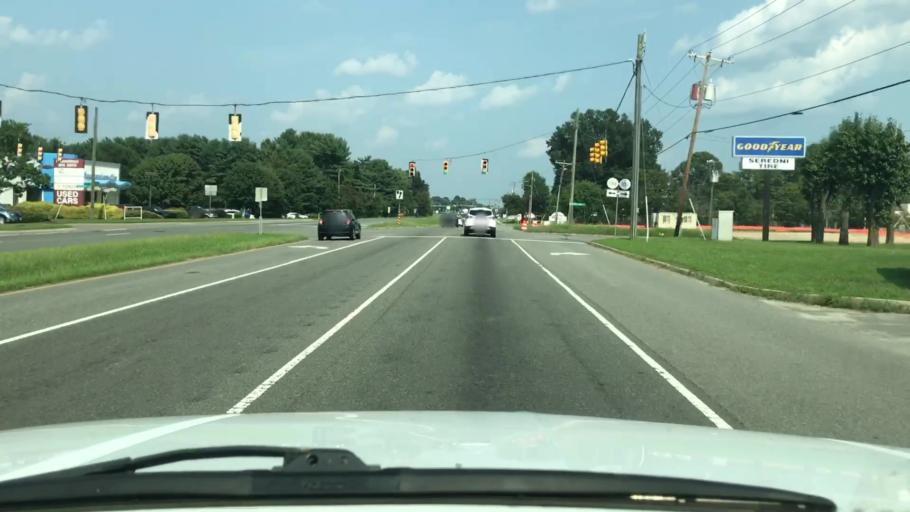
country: US
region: Virginia
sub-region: Hanover County
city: Mechanicsville
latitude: 37.6128
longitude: -77.3346
